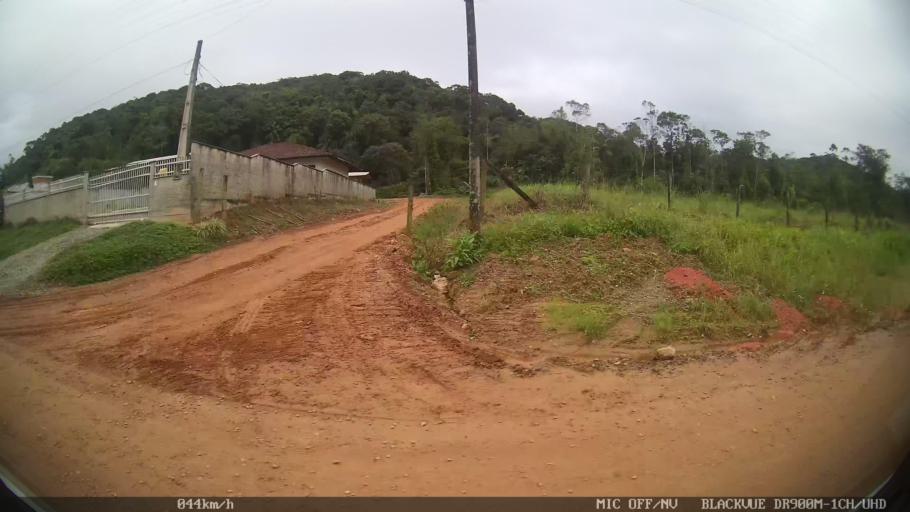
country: BR
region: Santa Catarina
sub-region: Joinville
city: Joinville
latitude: -26.2738
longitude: -48.9351
